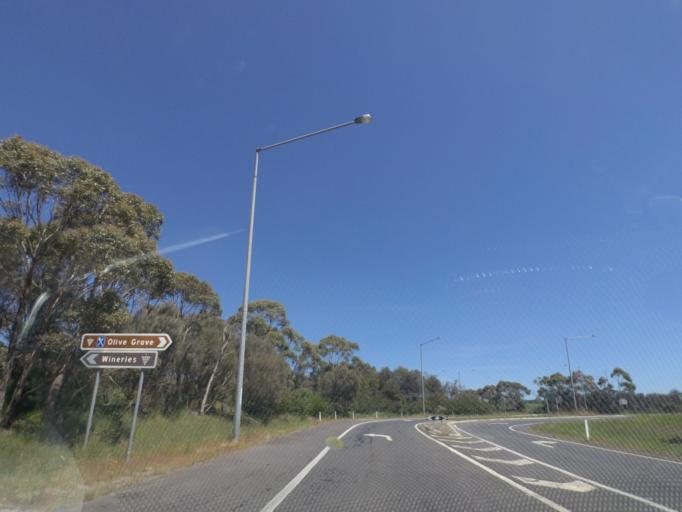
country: AU
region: Victoria
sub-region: Hume
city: Sunbury
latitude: -37.5410
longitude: 144.6424
